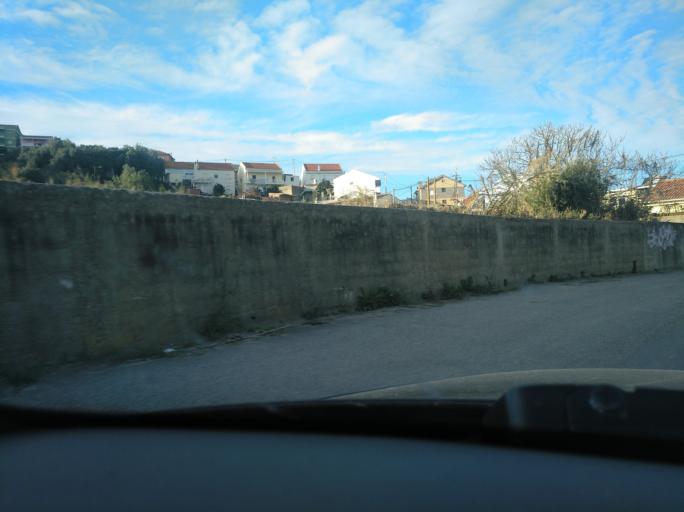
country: PT
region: Lisbon
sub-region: Loures
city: Unhos
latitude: 38.8303
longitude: -9.1217
